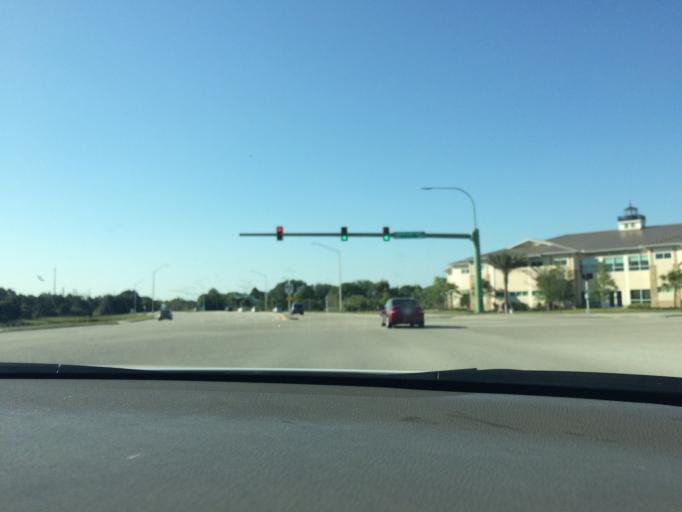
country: US
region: Florida
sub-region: Sarasota County
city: The Meadows
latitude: 27.4357
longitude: -82.4284
